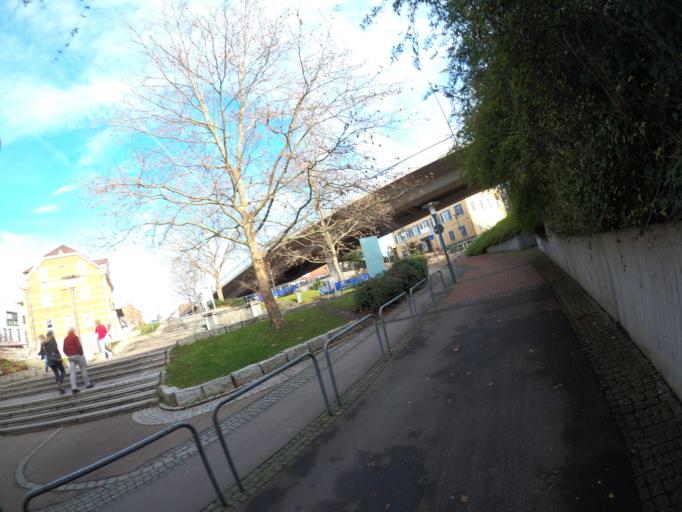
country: DE
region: Baden-Wuerttemberg
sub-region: Regierungsbezirk Stuttgart
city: Eislingen
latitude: 48.7011
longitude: 9.7041
